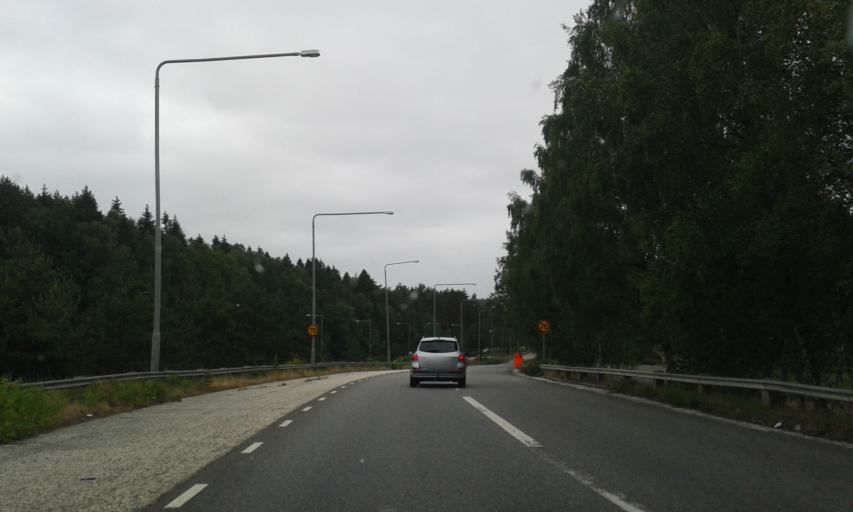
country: SE
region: Vaestra Goetaland
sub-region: Goteborg
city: Eriksbo
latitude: 57.7557
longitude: 12.0438
